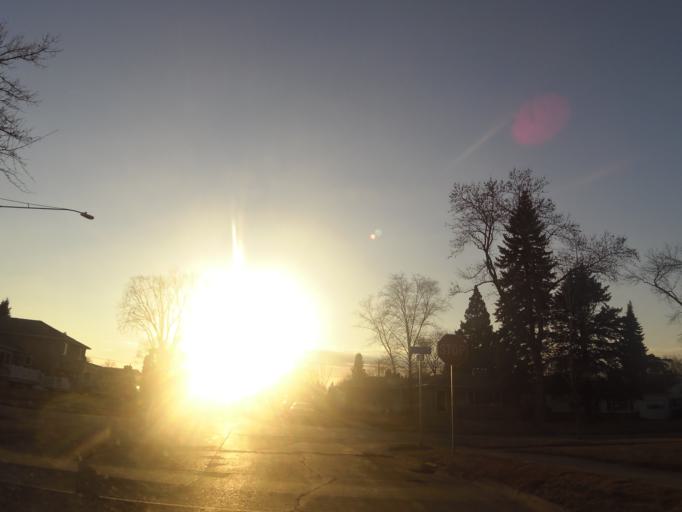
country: US
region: North Dakota
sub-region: Grand Forks County
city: Grand Forks
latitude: 47.8998
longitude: -97.0303
